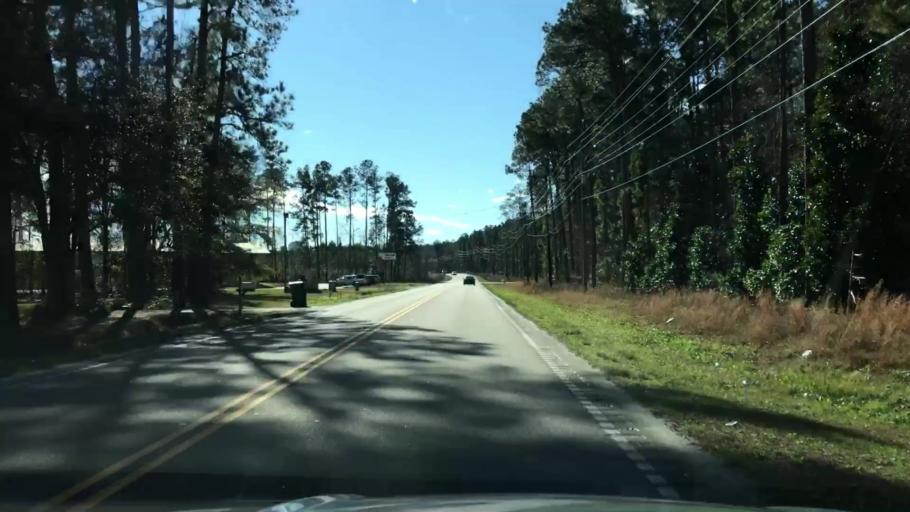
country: US
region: South Carolina
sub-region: Dorchester County
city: Summerville
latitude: 33.0772
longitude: -80.2139
